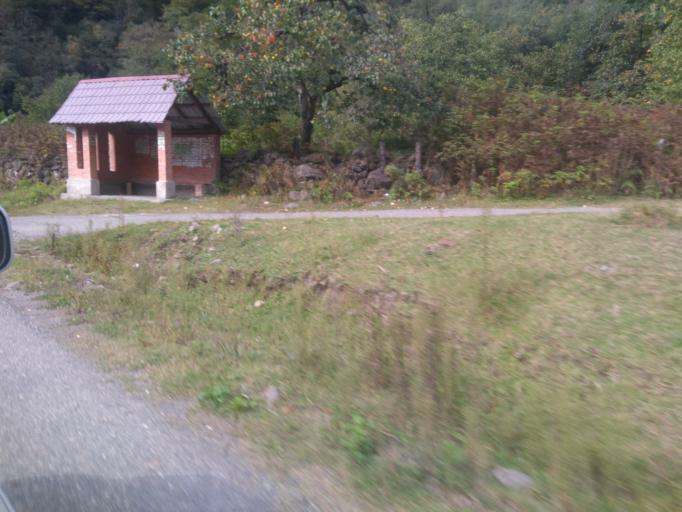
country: TR
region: Artvin
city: Muratli
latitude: 41.5478
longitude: 41.7594
